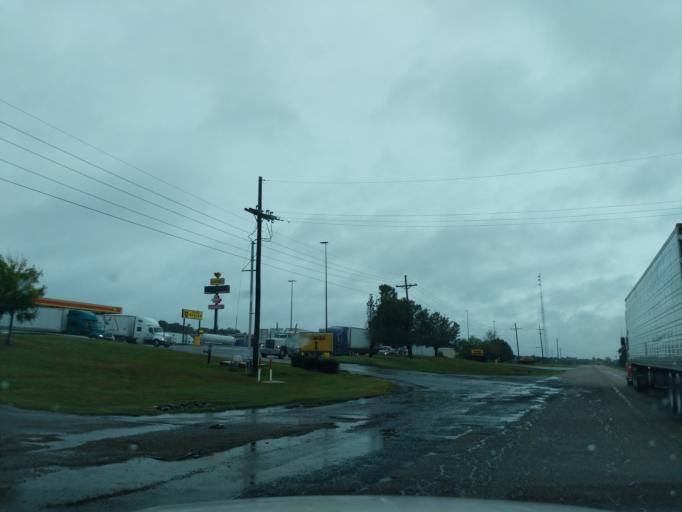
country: US
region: Louisiana
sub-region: Webster Parish
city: Minden
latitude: 32.5828
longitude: -93.2486
